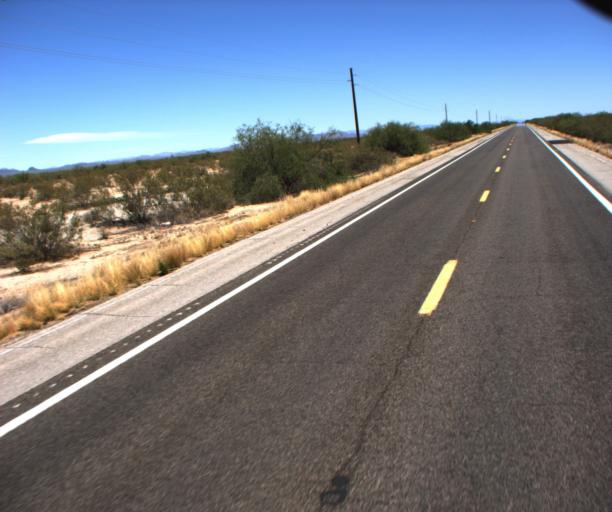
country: US
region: Arizona
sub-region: La Paz County
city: Salome
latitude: 33.8866
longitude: -113.3459
